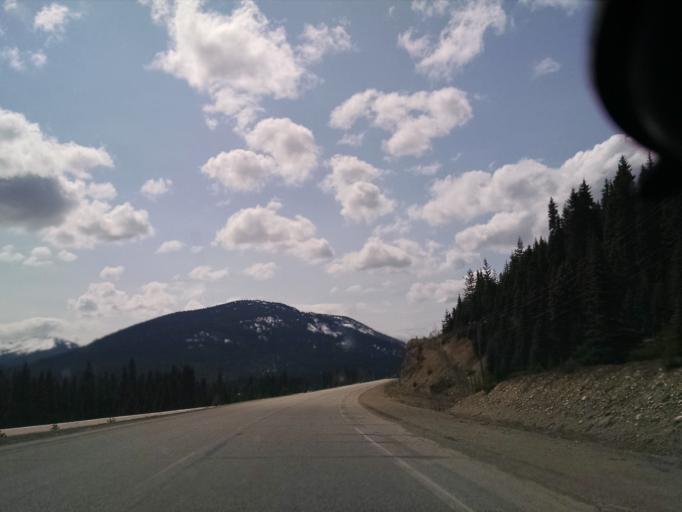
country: CA
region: British Columbia
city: Hope
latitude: 49.6416
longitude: -121.0027
